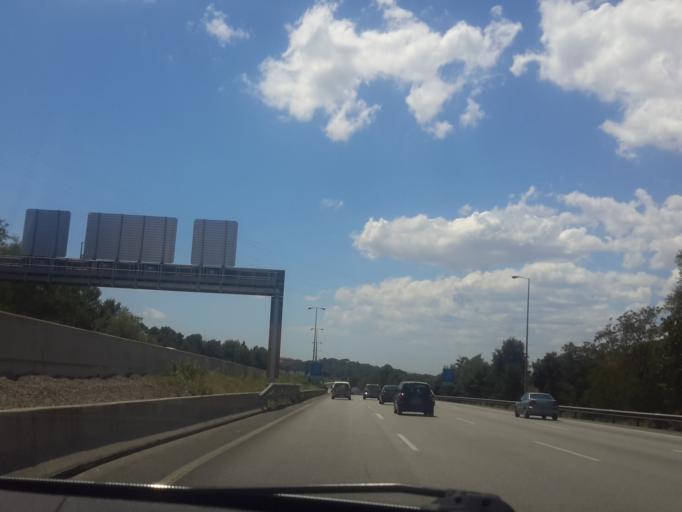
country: ES
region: Catalonia
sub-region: Provincia de Barcelona
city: Granollers
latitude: 41.5902
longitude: 2.3068
